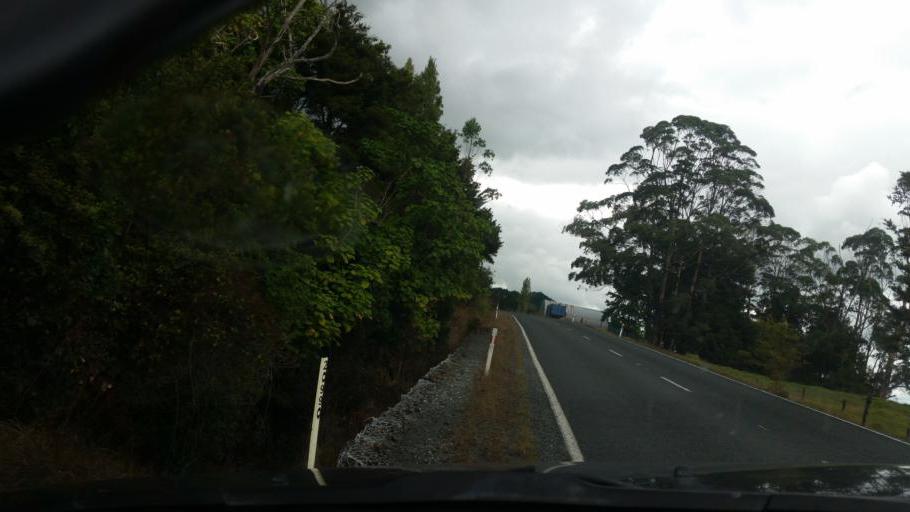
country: NZ
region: Northland
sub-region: Whangarei
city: Ruakaka
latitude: -35.9451
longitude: 174.2919
